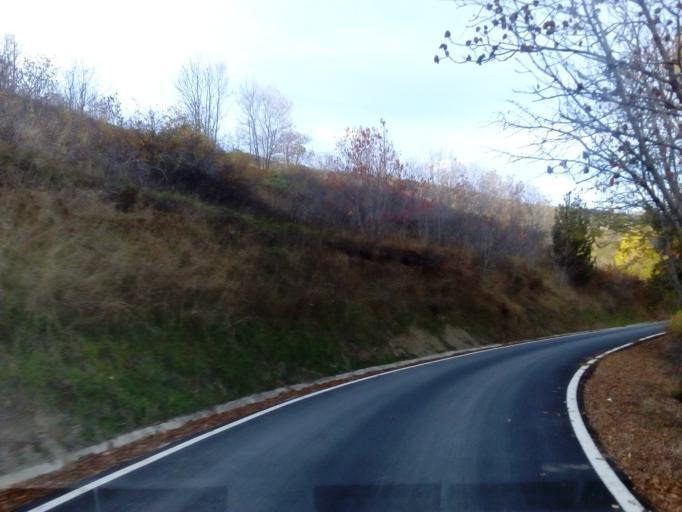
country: ES
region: Catalonia
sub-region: Provincia de Lleida
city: Eller
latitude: 42.4134
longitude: 1.7938
